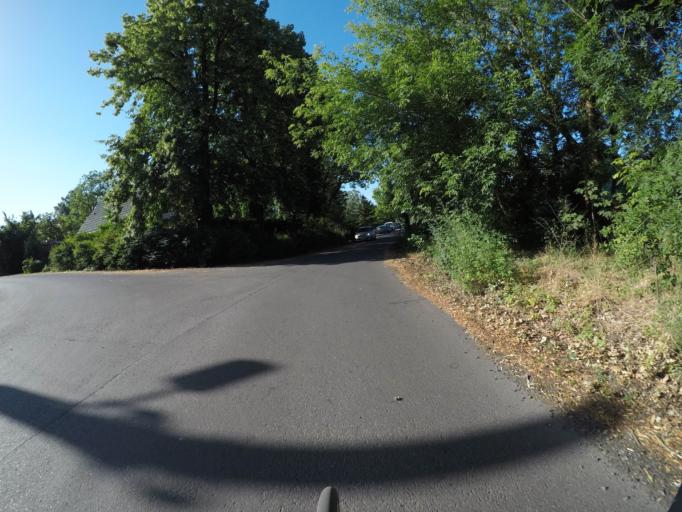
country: DE
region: Brandenburg
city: Wildau
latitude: 52.3426
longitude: 13.6469
